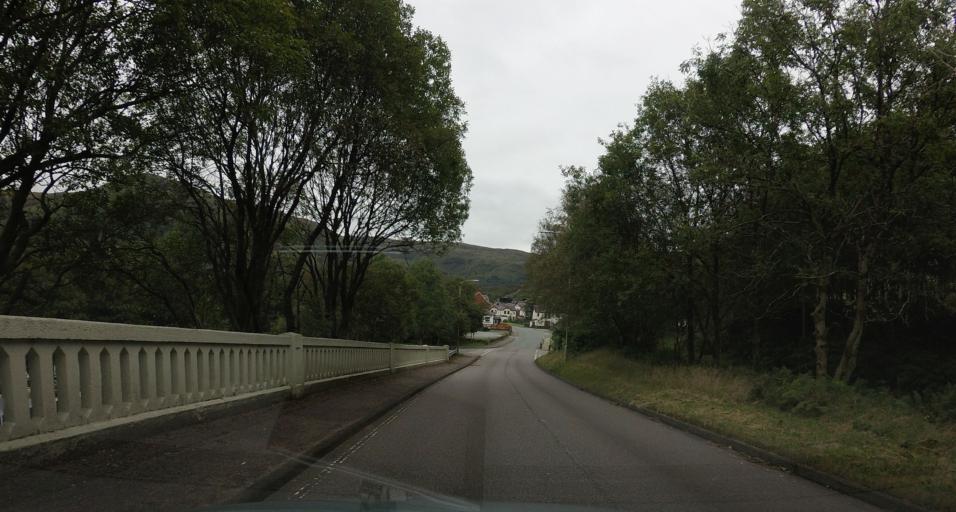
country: GB
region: Scotland
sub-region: Highland
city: Fort William
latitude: 56.7132
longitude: -4.9692
